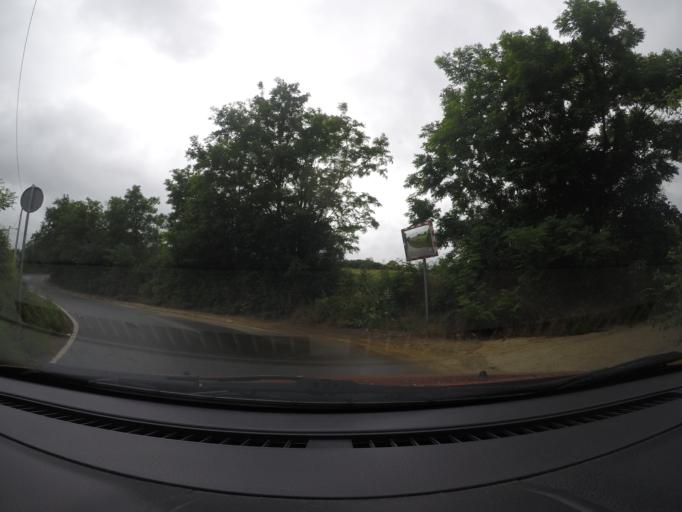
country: RS
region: Central Serbia
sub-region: Belgrade
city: Zvezdara
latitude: 44.7050
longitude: 20.5647
